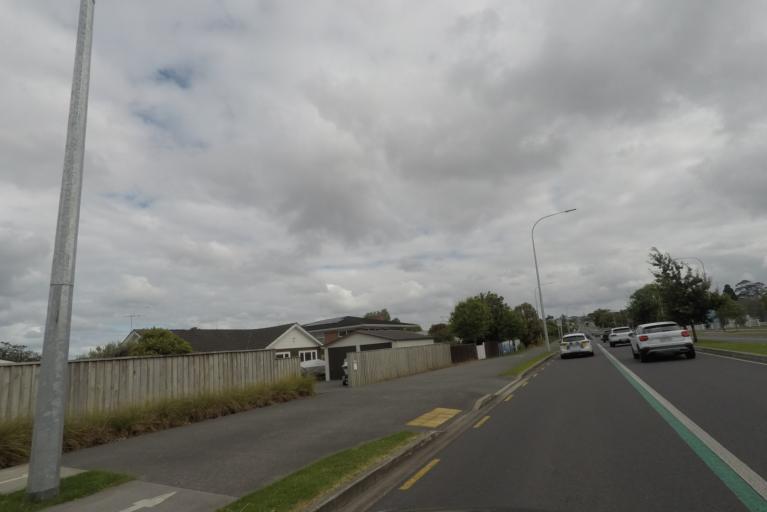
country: NZ
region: Auckland
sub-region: Auckland
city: Rothesay Bay
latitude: -36.7407
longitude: 174.6927
